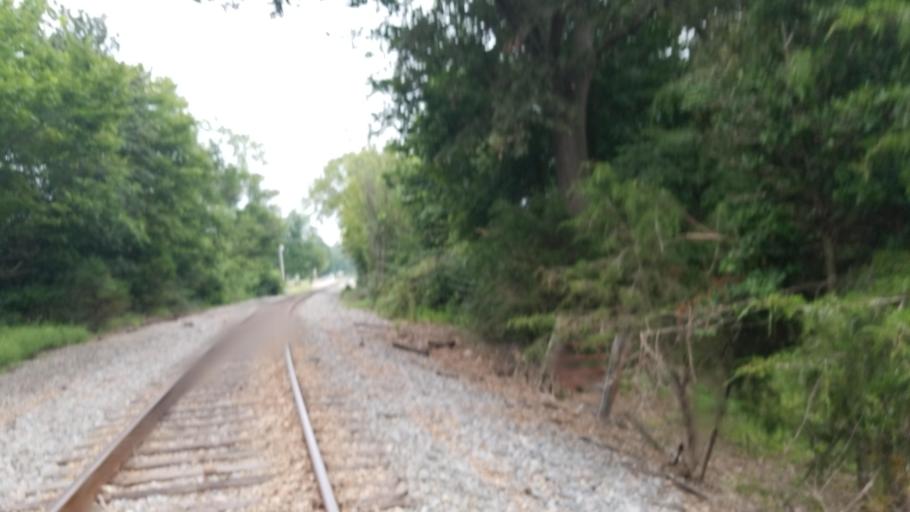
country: US
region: Illinois
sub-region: Saline County
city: Harrisburg
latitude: 37.8378
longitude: -88.6147
